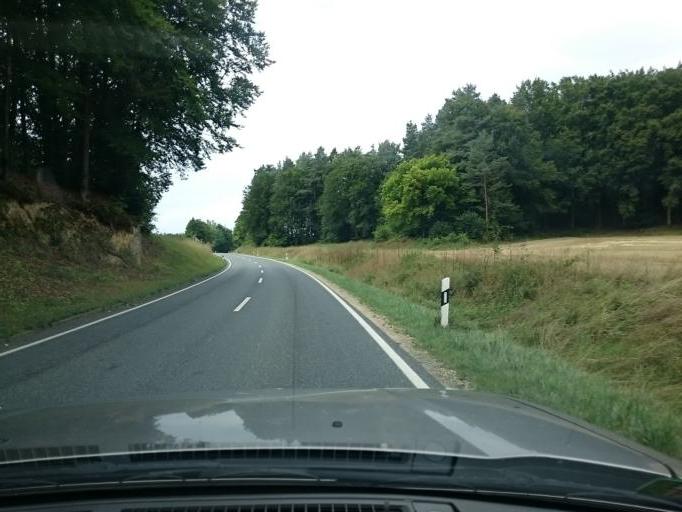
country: DE
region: Bavaria
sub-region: Regierungsbezirk Mittelfranken
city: Velden
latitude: 49.6447
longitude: 11.5000
